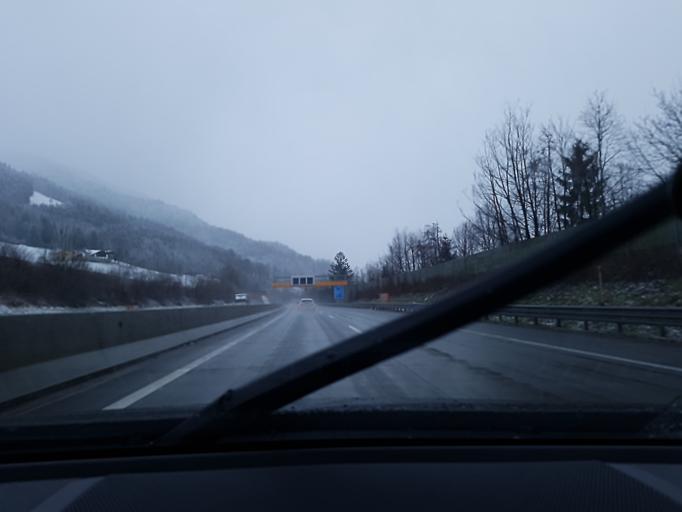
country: AT
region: Salzburg
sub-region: Politischer Bezirk Hallein
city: Kuchl
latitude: 47.6095
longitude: 13.1447
